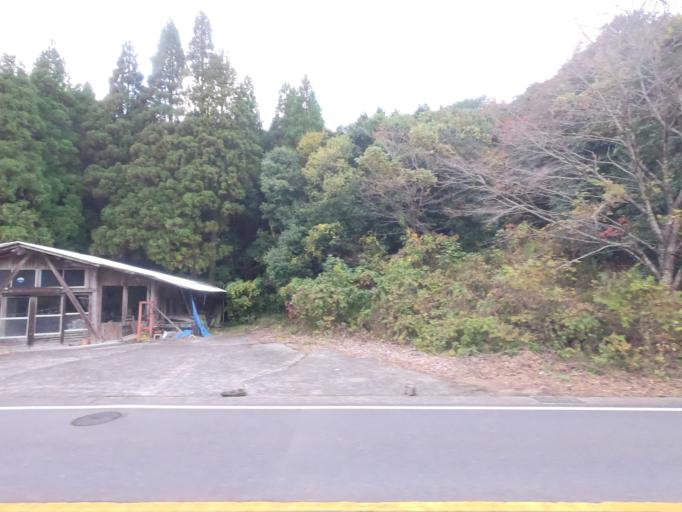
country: JP
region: Kumamoto
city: Minamata
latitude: 32.2536
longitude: 130.5046
